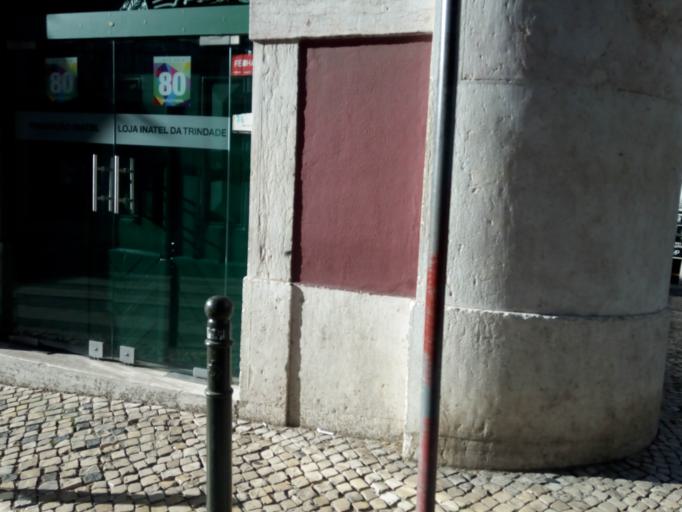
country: PT
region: Lisbon
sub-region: Lisbon
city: Lisbon
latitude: 38.7120
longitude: -9.1425
